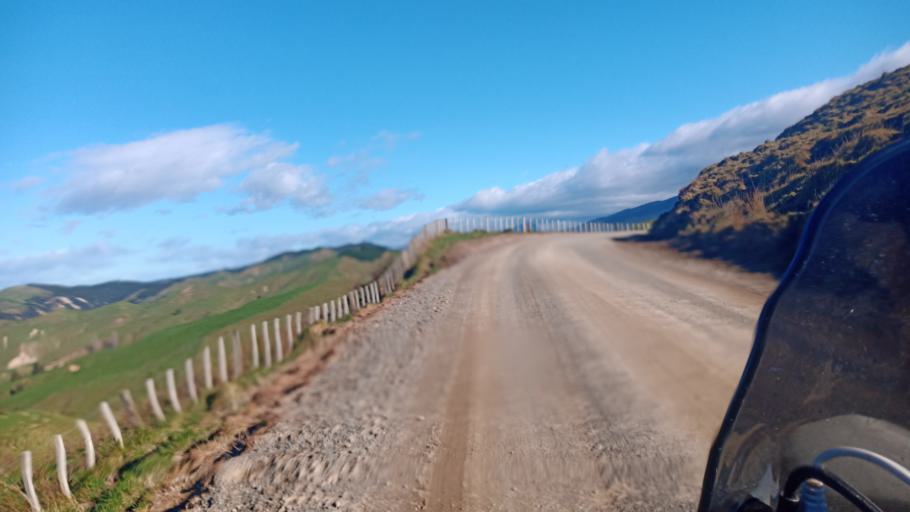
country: NZ
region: Hawke's Bay
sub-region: Wairoa District
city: Wairoa
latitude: -38.7848
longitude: 177.2699
